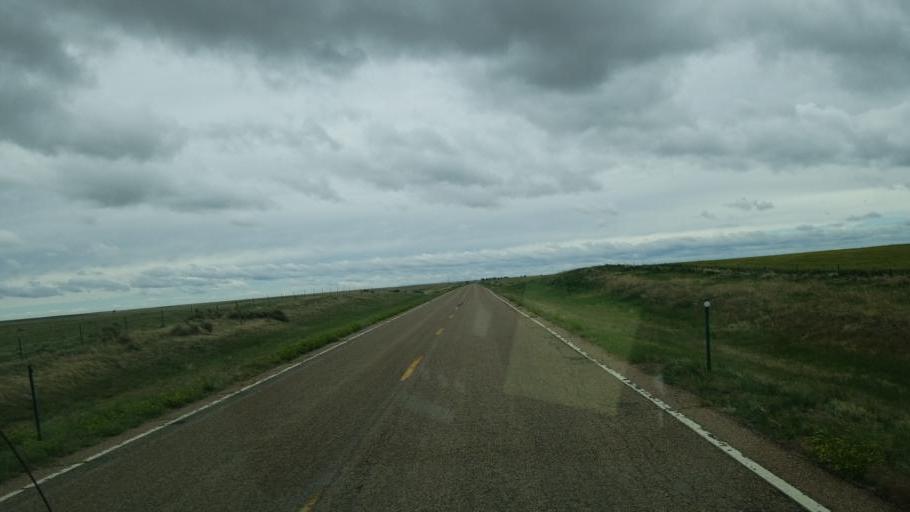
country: US
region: Colorado
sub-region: Lincoln County
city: Hugo
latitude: 38.8518
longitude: -103.6638
